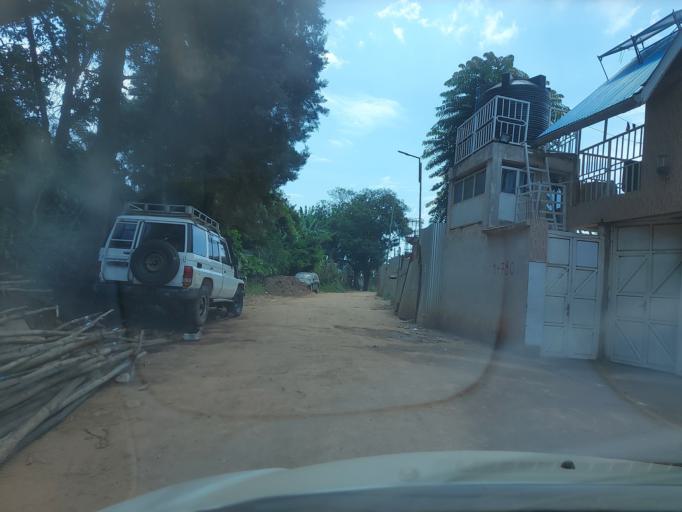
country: CD
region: South Kivu
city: Bukavu
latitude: -2.4962
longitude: 28.8622
